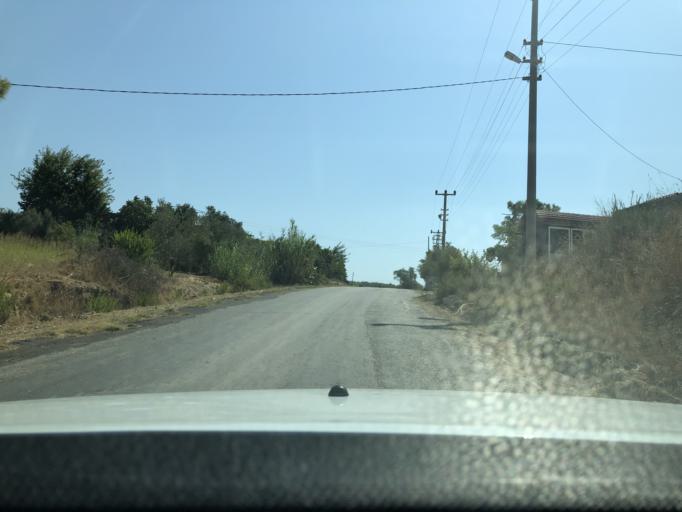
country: TR
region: Antalya
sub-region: Manavgat
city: Manavgat
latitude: 36.8219
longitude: 31.4998
